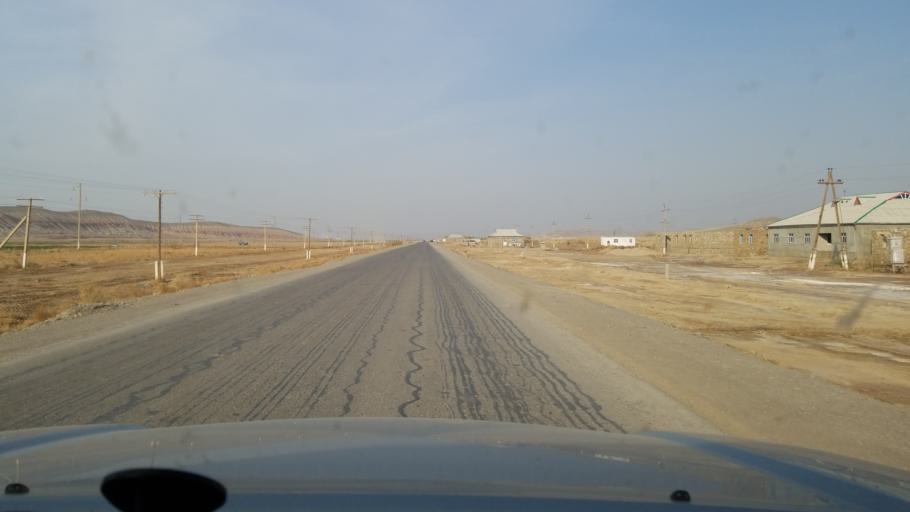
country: AF
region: Jowzjan
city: Qarqin
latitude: 37.5245
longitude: 66.0493
